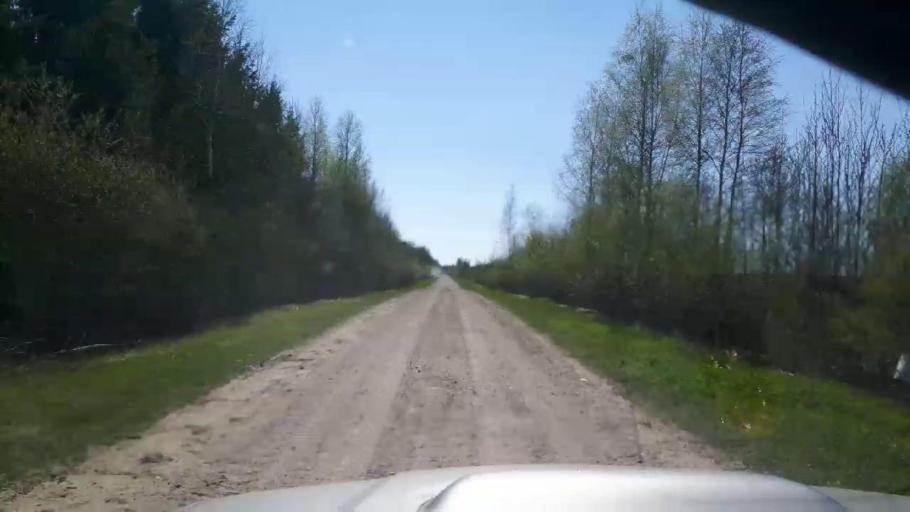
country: EE
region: Paernumaa
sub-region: Tootsi vald
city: Tootsi
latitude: 58.4720
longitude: 24.8166
